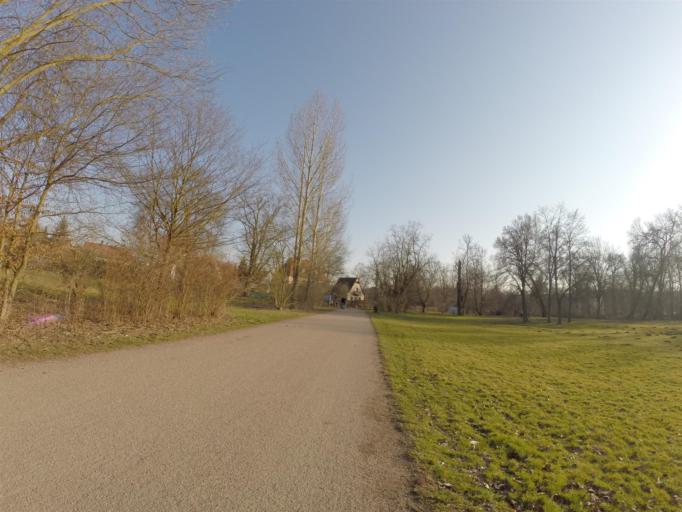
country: DE
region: Thuringia
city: Weimar
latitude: 50.9671
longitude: 11.3417
